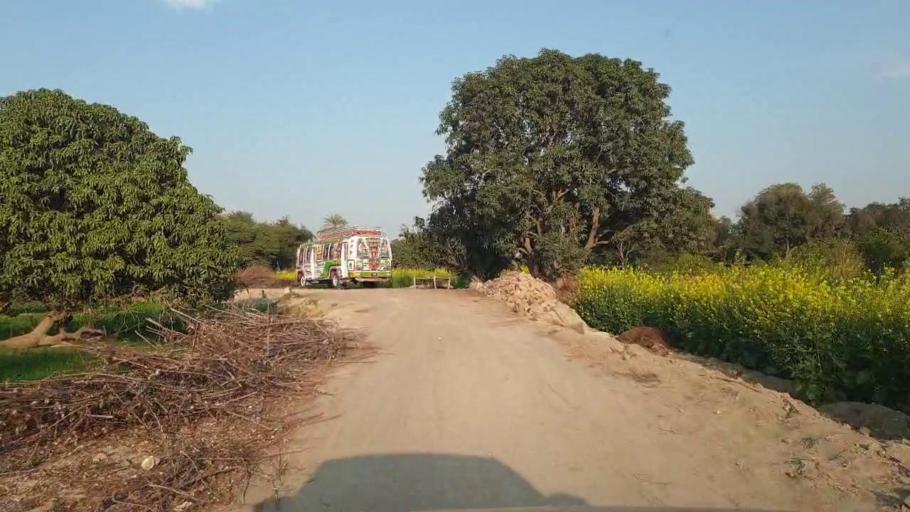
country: PK
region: Sindh
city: Shahpur Chakar
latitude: 26.1498
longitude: 68.6369
